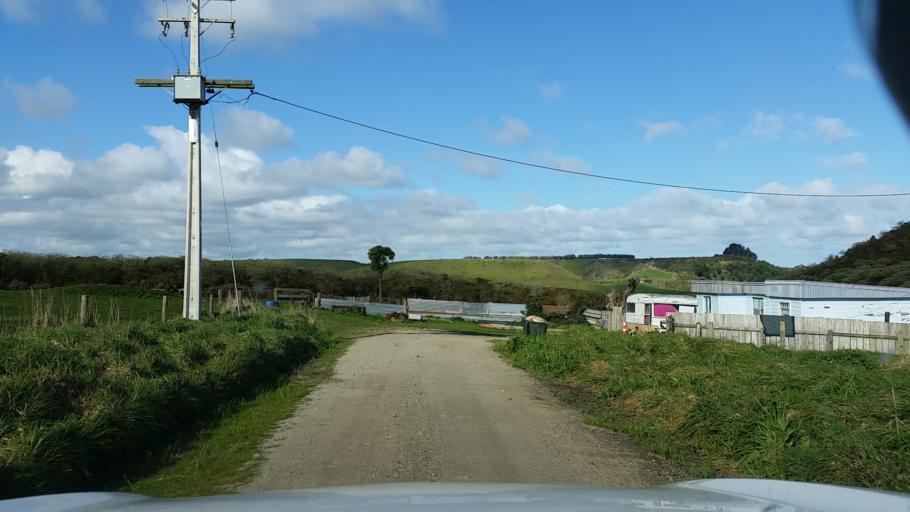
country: NZ
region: Taranaki
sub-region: South Taranaki District
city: Patea
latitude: -39.7204
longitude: 174.4713
